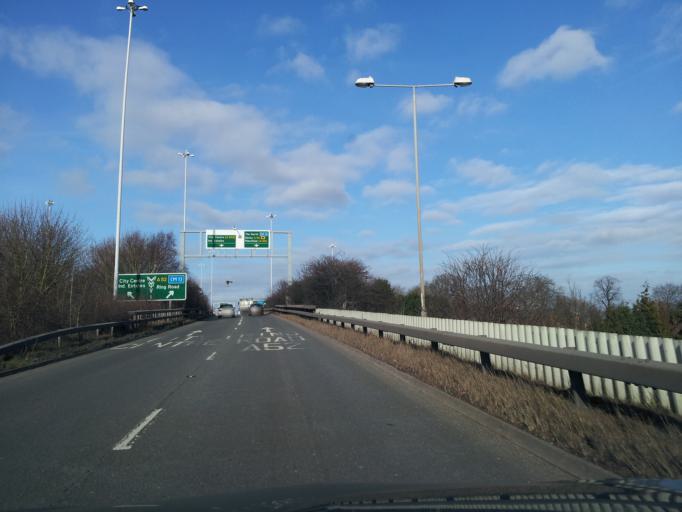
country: GB
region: England
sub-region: Nottinghamshire
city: Ruddington
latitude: 52.9211
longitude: -1.1632
